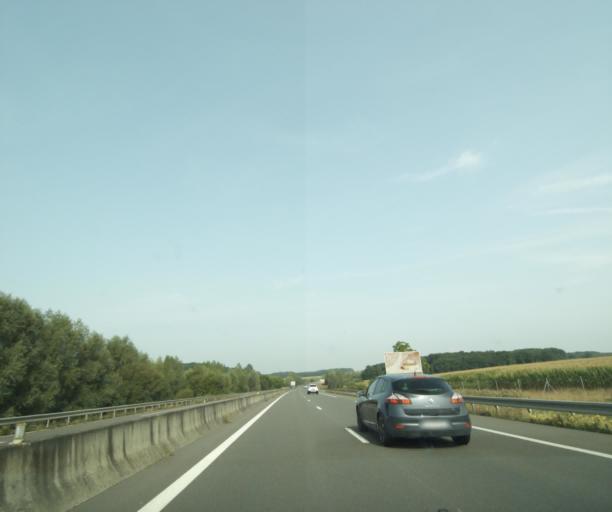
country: FR
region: Pays de la Loire
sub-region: Departement de la Sarthe
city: Champfleur
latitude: 48.3291
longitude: 0.1133
